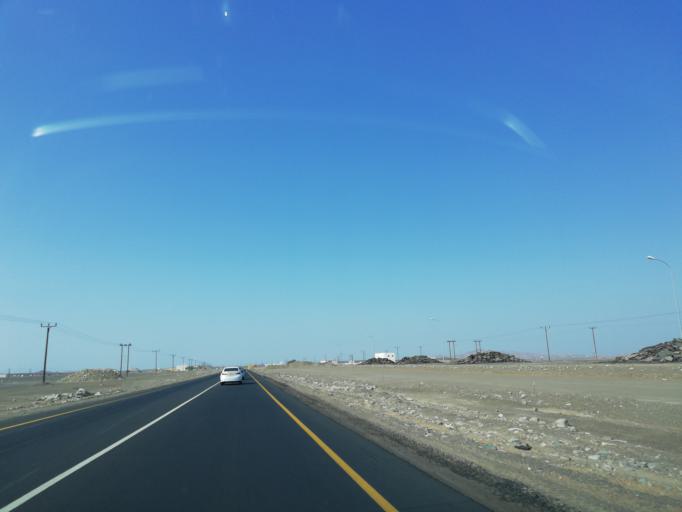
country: OM
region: Ash Sharqiyah
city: Ibra'
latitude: 22.7090
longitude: 58.1434
